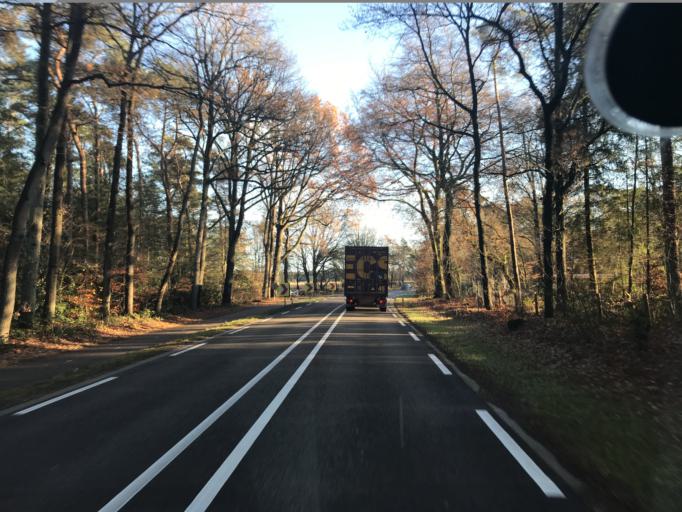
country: NL
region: Gelderland
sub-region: Gemeente Ermelo
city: Ermelo
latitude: 52.3150
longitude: 5.6704
